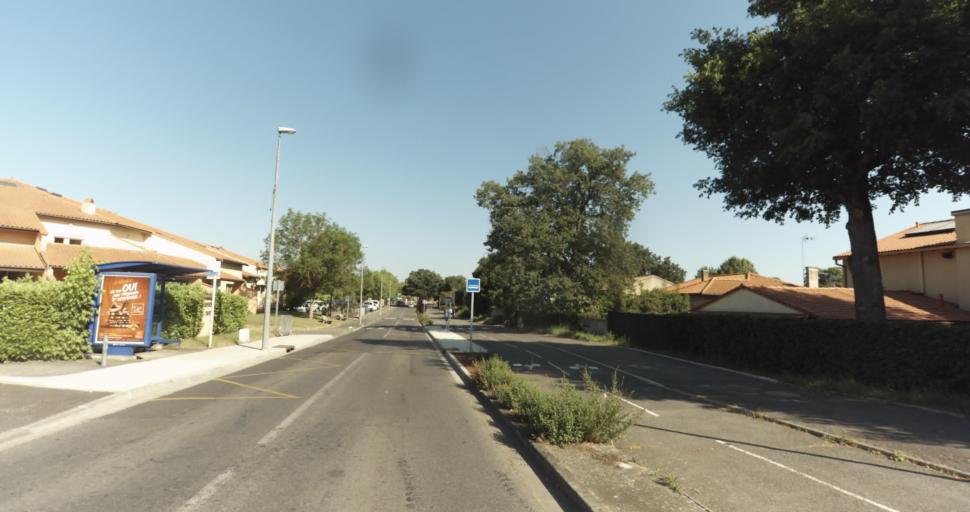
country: FR
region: Midi-Pyrenees
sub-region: Departement de la Haute-Garonne
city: Plaisance-du-Touch
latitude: 43.5637
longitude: 1.2995
